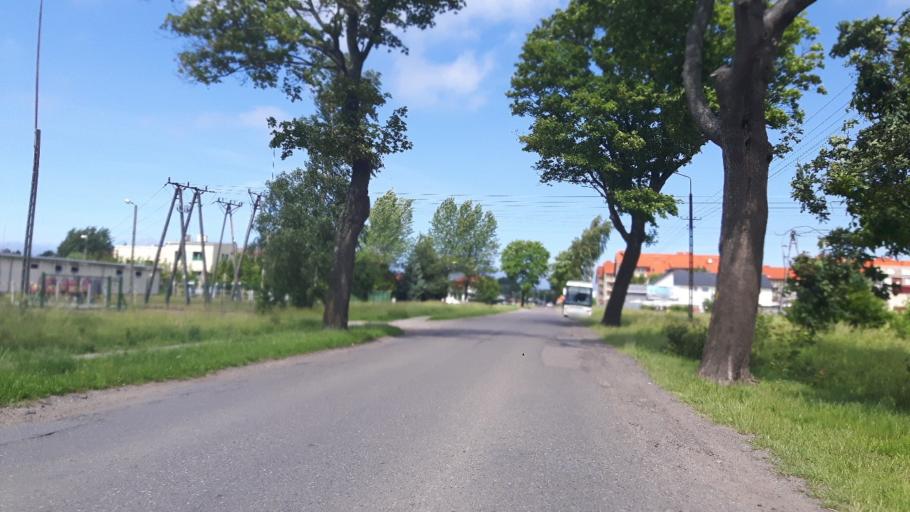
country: PL
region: Pomeranian Voivodeship
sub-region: Powiat slupski
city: Ustka
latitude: 54.5709
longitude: 16.8510
